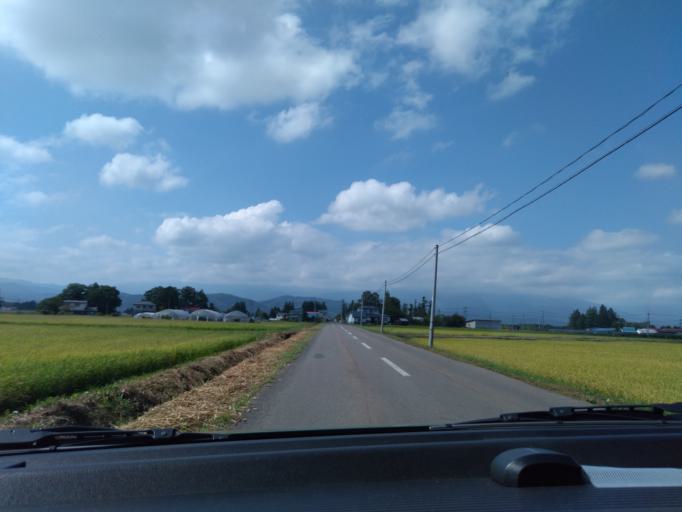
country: JP
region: Iwate
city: Shizukuishi
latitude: 39.6746
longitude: 140.9647
